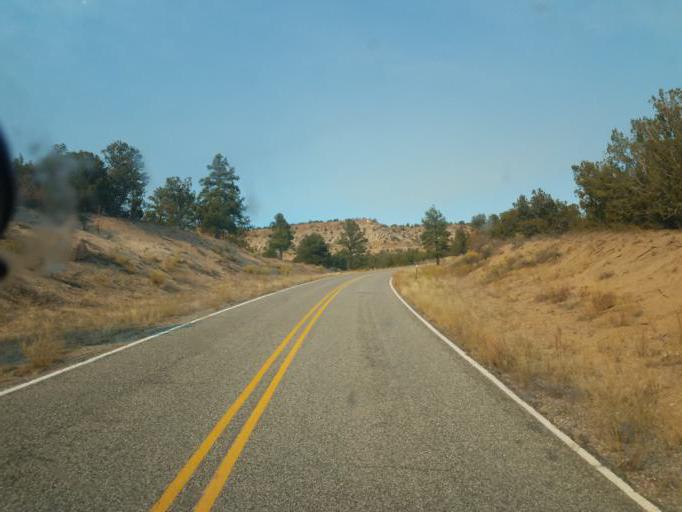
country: US
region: New Mexico
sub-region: Los Alamos County
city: White Rock
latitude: 35.8078
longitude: -106.2488
